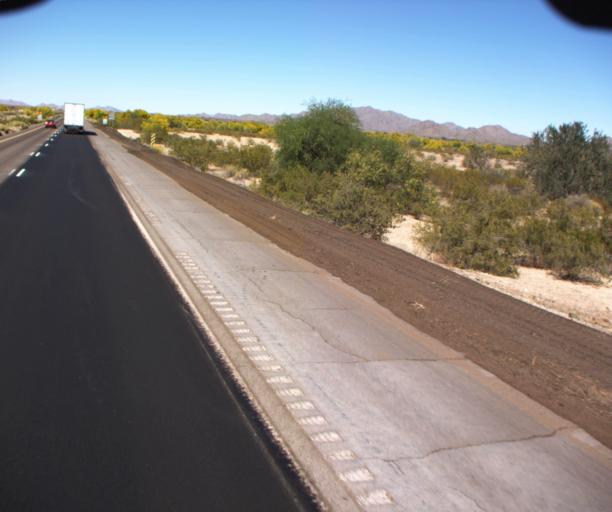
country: US
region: Arizona
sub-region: Maricopa County
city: Gila Bend
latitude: 33.0706
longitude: -112.6458
